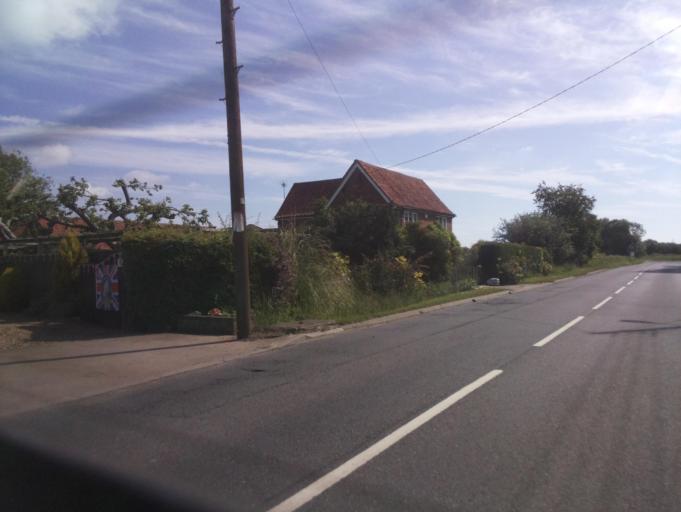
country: GB
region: England
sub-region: Lincolnshire
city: Skellingthorpe
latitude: 53.1563
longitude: -0.6304
